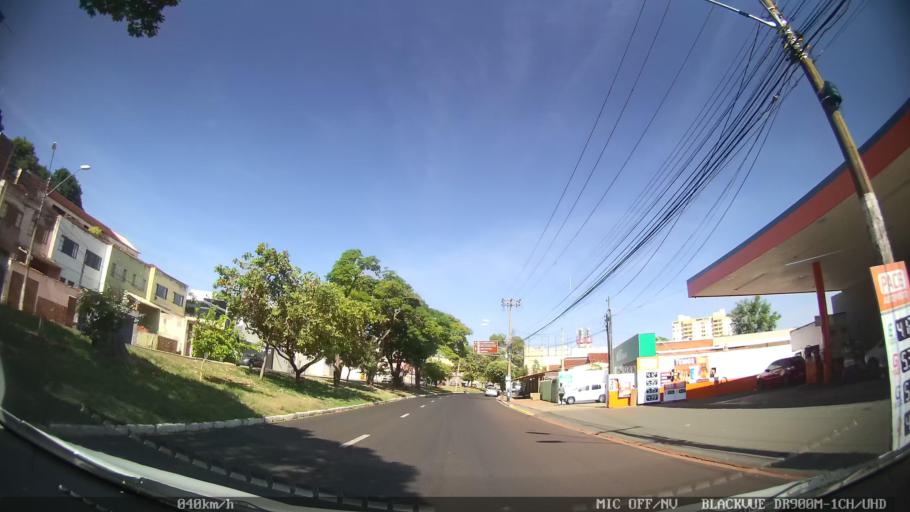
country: BR
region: Sao Paulo
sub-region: Ribeirao Preto
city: Ribeirao Preto
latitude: -21.1818
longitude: -47.8183
